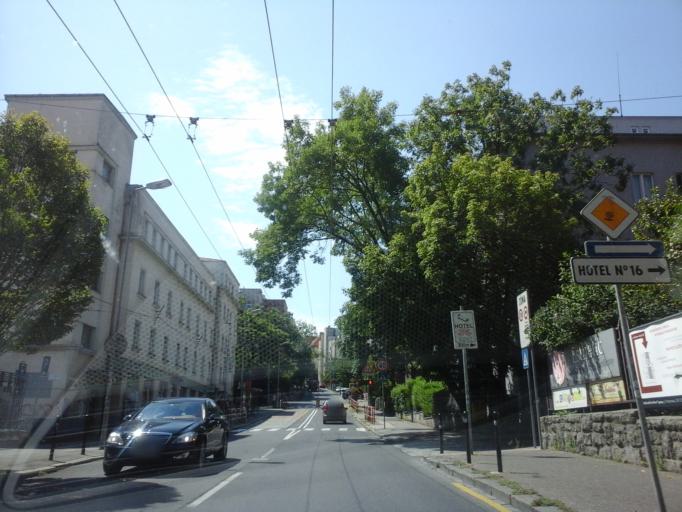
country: SK
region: Bratislavsky
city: Bratislava
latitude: 48.1462
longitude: 17.0993
